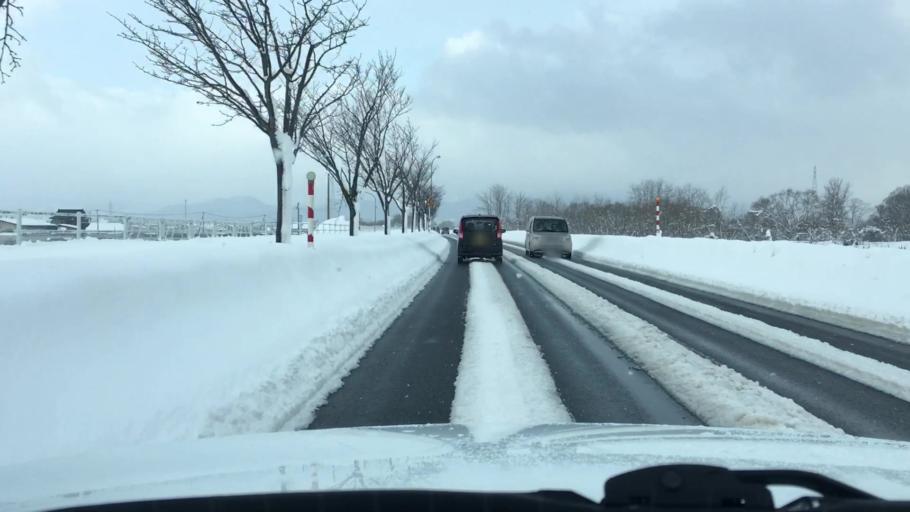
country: JP
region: Aomori
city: Hirosaki
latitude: 40.6359
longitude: 140.4718
